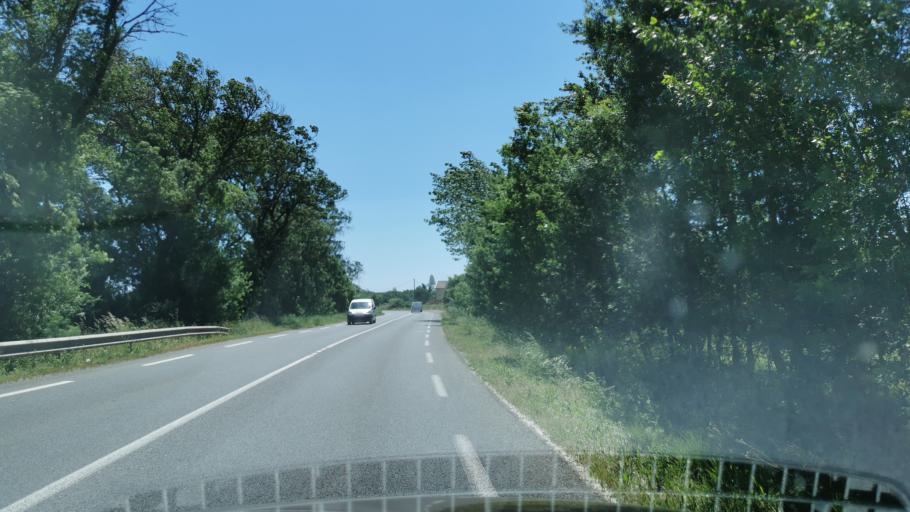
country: FR
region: Languedoc-Roussillon
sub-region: Departement de l'Aude
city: Narbonne
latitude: 43.2172
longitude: 3.0113
